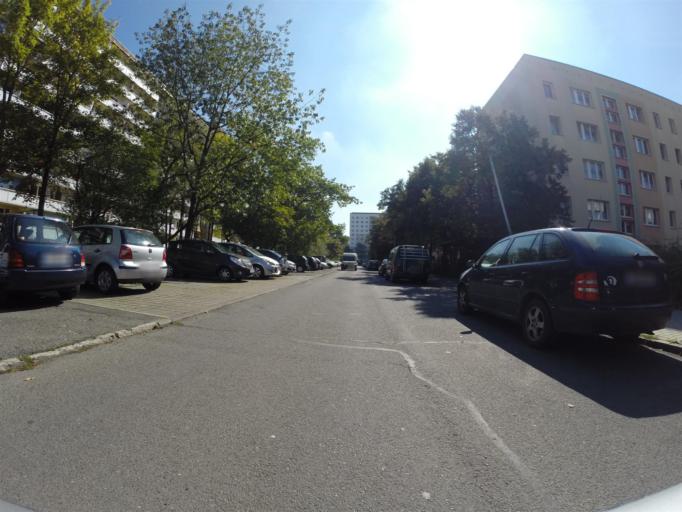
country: DE
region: Thuringia
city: Sulza
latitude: 50.8838
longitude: 11.6098
